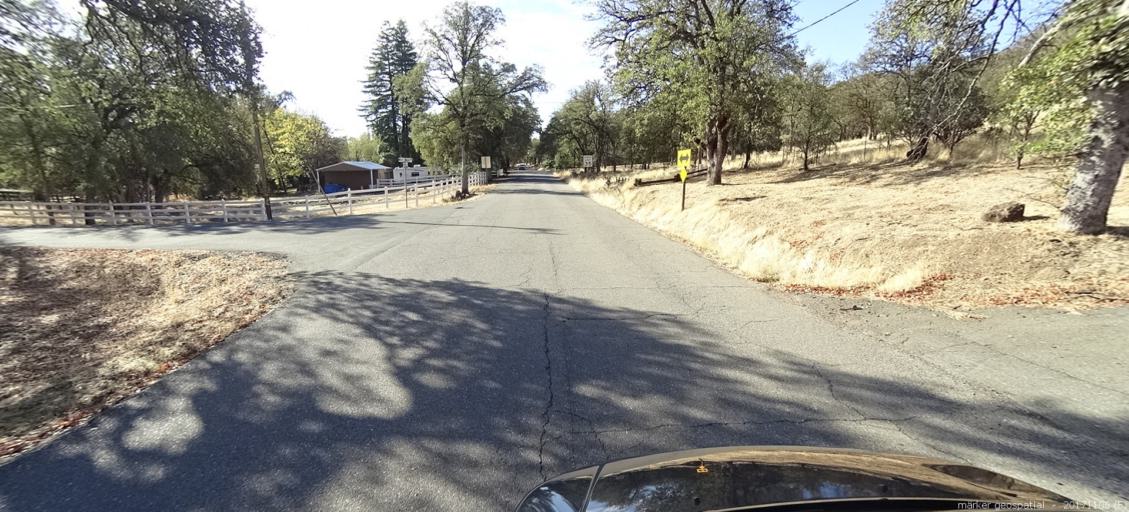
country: US
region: California
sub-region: Shasta County
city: Palo Cedro
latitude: 40.5437
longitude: -122.2479
